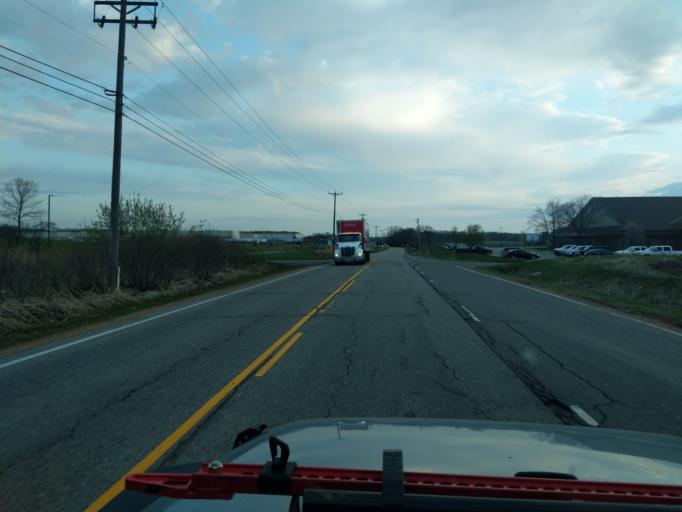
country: US
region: Minnesota
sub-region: Hennepin County
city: Rogers
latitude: 45.1736
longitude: -93.5216
